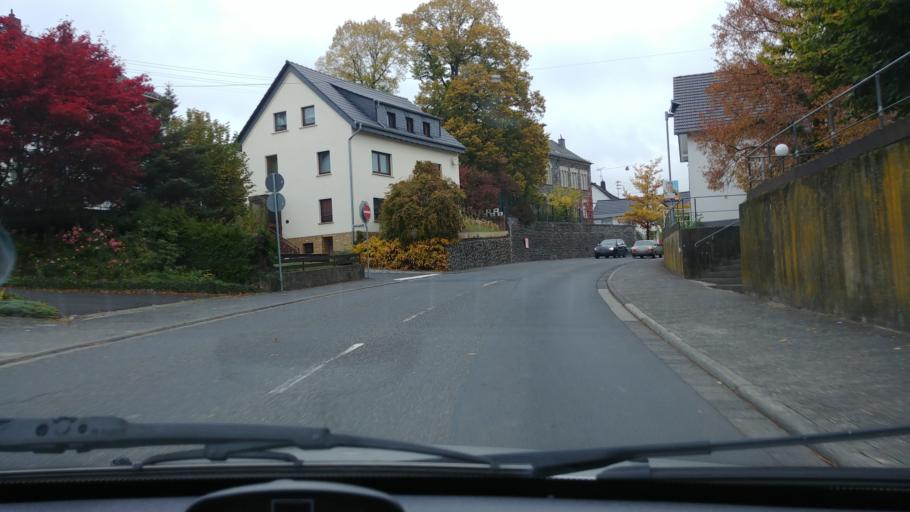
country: DE
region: Rheinland-Pfalz
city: Irmtraut
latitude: 50.5390
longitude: 8.0445
